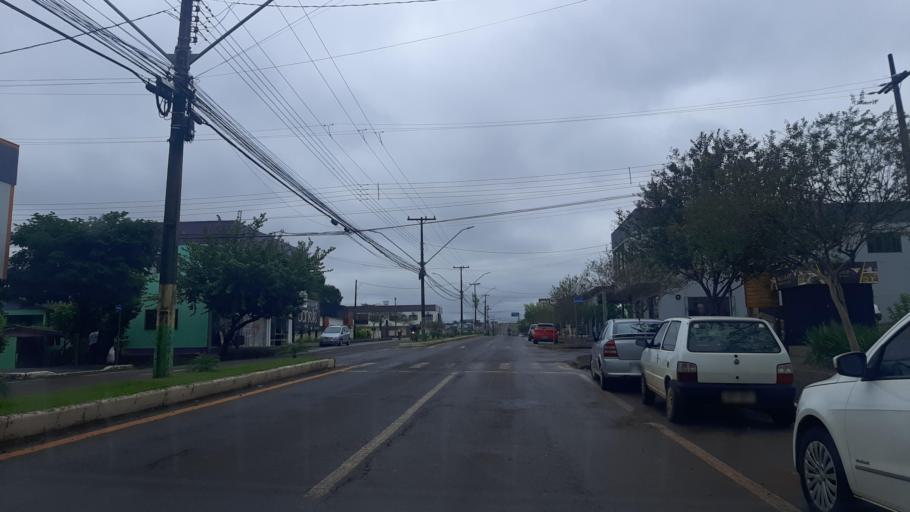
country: BR
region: Parana
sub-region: Santo Antonio Do Sudoeste
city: Santo Antonio do Sudoeste
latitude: -26.0606
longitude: -53.7262
